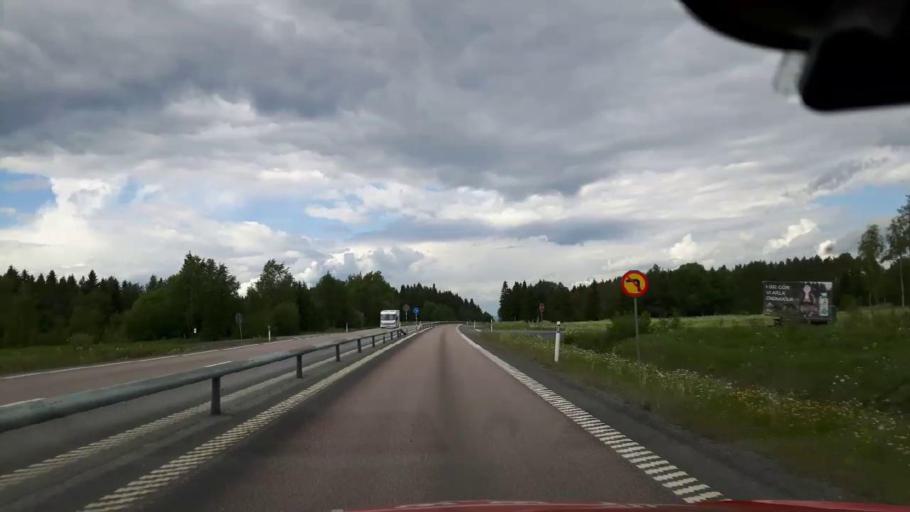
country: SE
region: Jaemtland
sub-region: OEstersunds Kommun
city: Ostersund
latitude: 63.2610
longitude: 14.5490
